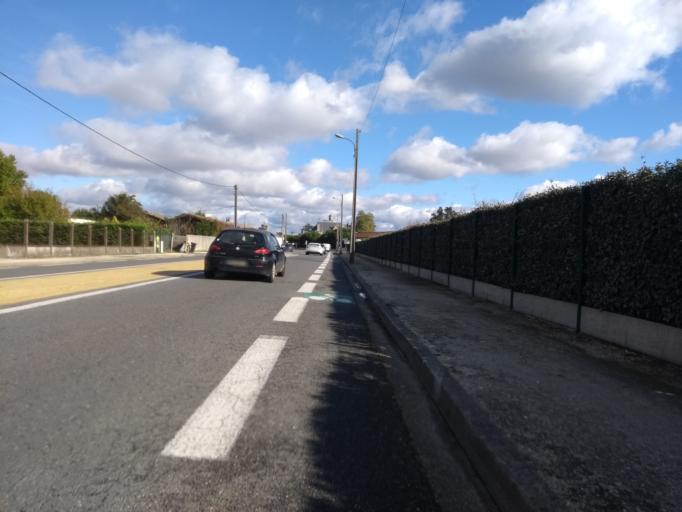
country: FR
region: Aquitaine
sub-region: Departement de la Gironde
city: Pessac
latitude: 44.8054
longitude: -0.6508
